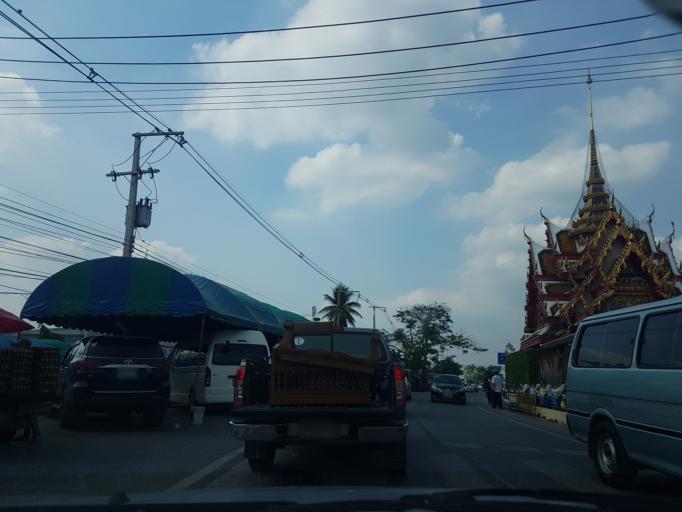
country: TH
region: Phra Nakhon Si Ayutthaya
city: Phachi
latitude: 14.3966
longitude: 100.7932
